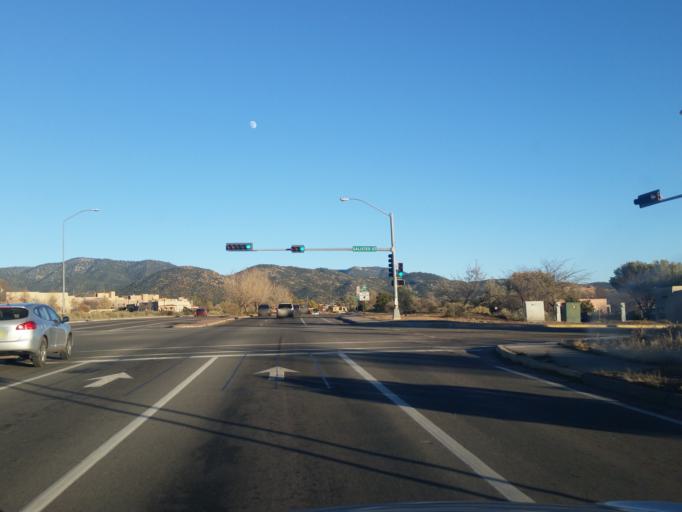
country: US
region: New Mexico
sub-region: Santa Fe County
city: Santa Fe
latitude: 35.6586
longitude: -105.9522
